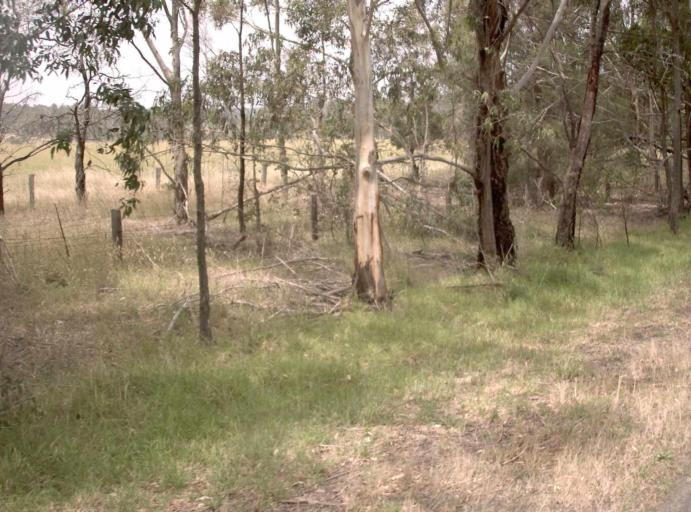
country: AU
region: Victoria
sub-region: Latrobe
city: Traralgon
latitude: -38.4887
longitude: 146.7137
